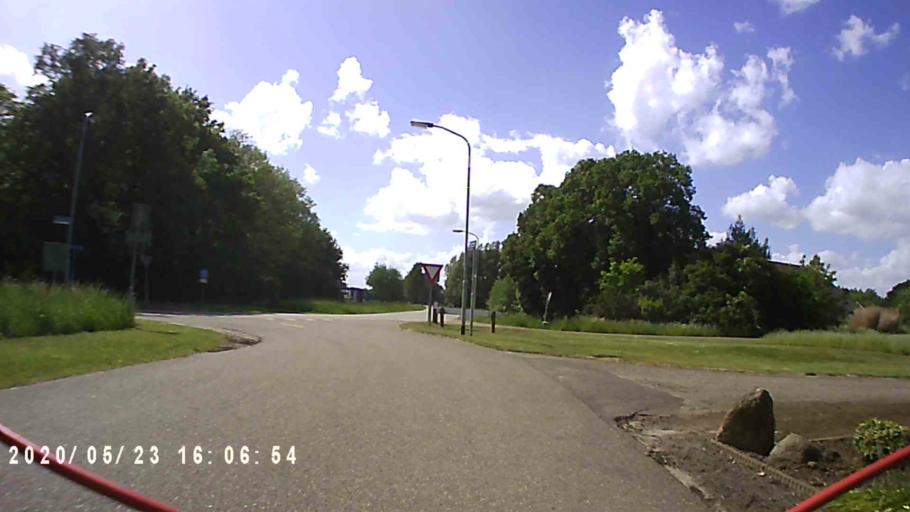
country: NL
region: Groningen
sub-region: Gemeente Appingedam
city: Appingedam
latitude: 53.2468
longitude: 6.8905
